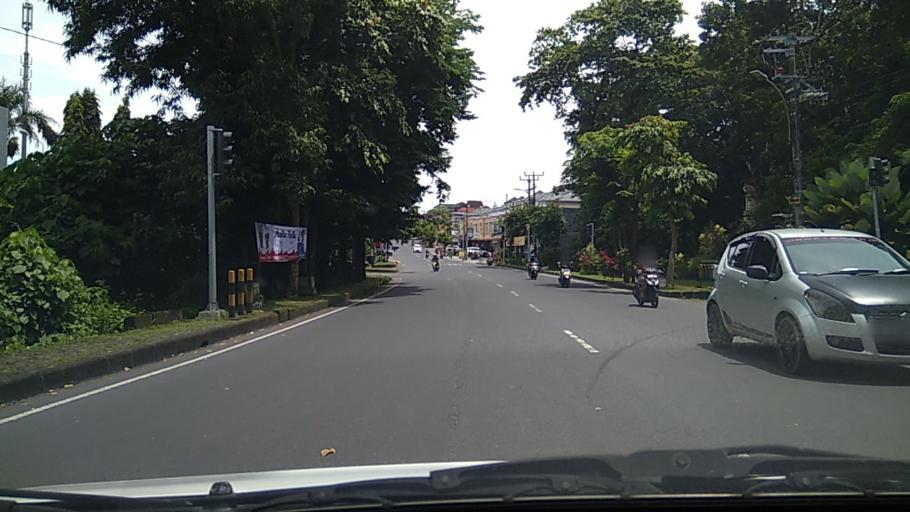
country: ID
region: Bali
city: Tabanan
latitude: -8.5433
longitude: 115.1395
